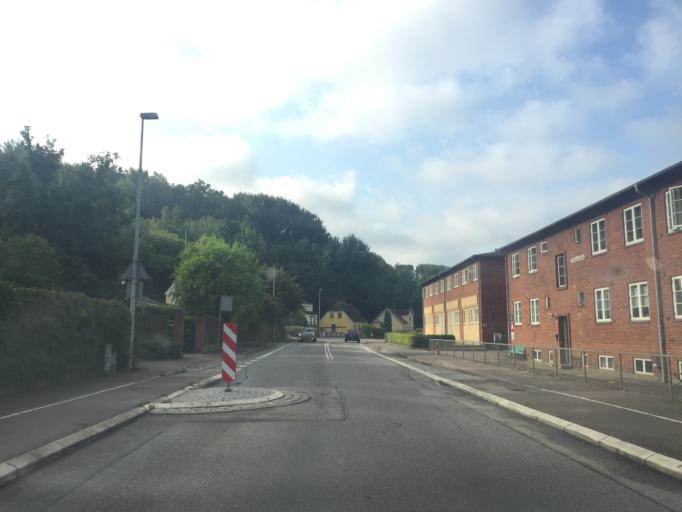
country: DK
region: Capital Region
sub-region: Halsnaes Kommune
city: Frederiksvaerk
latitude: 55.9632
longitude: 12.0215
